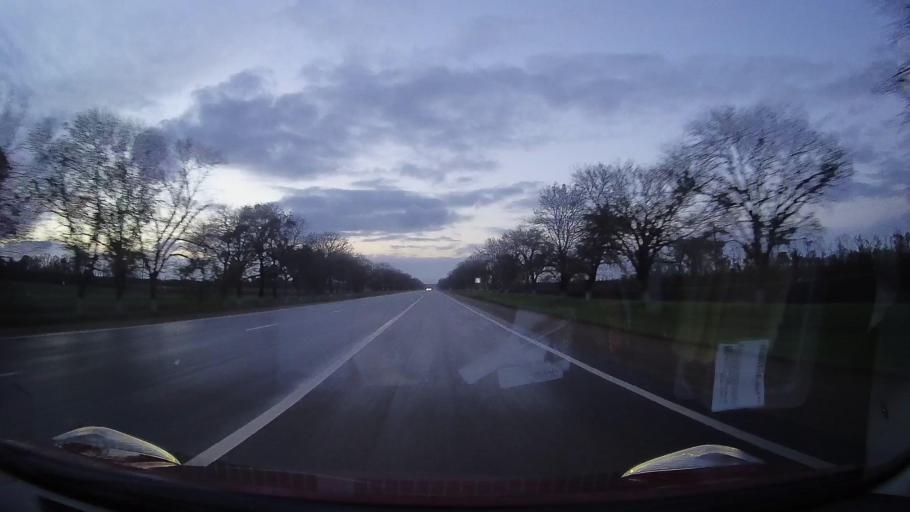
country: RU
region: Krasnodarskiy
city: Zavetnyy
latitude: 44.9011
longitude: 41.1842
